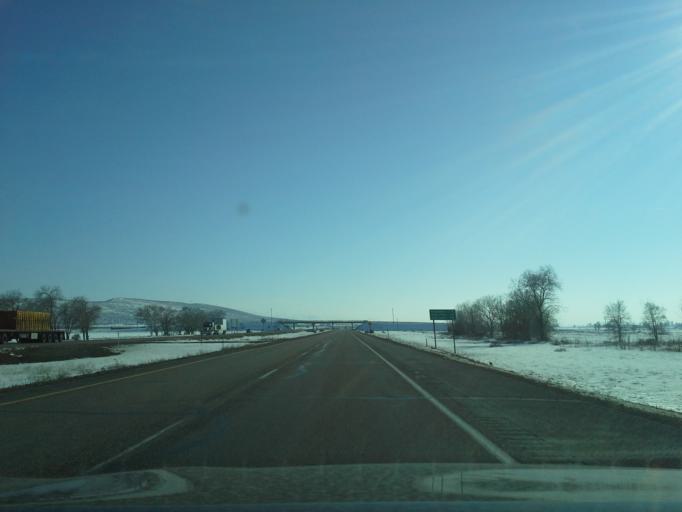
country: US
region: Idaho
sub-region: Bingham County
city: Blackfoot
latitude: 43.1432
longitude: -112.3889
